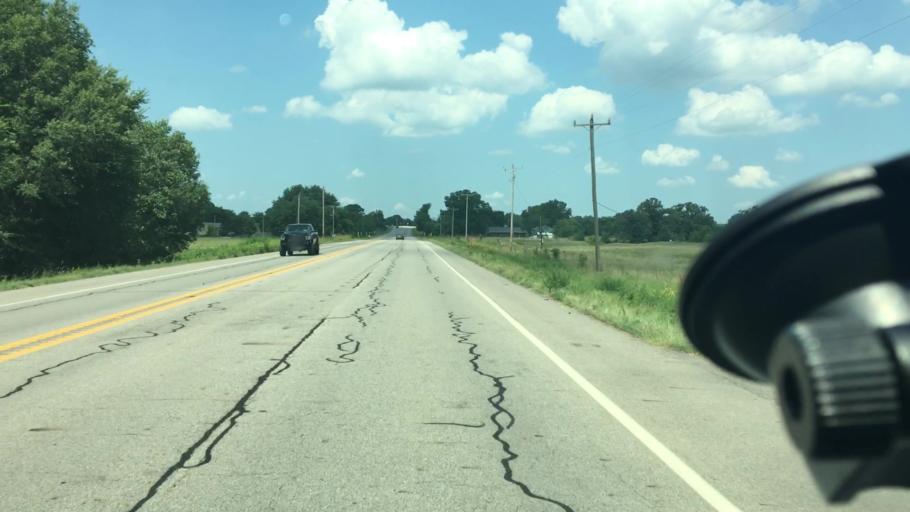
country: US
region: Arkansas
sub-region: Logan County
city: Paris
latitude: 35.2986
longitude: -93.8188
